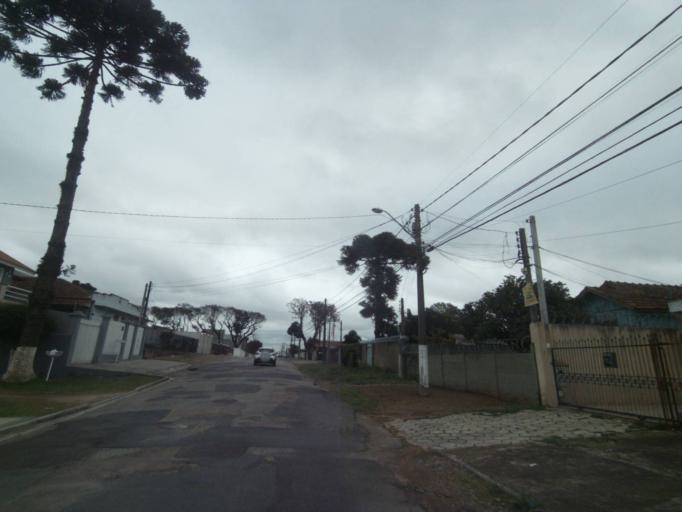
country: BR
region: Parana
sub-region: Sao Jose Dos Pinhais
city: Sao Jose dos Pinhais
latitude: -25.5178
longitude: -49.3014
